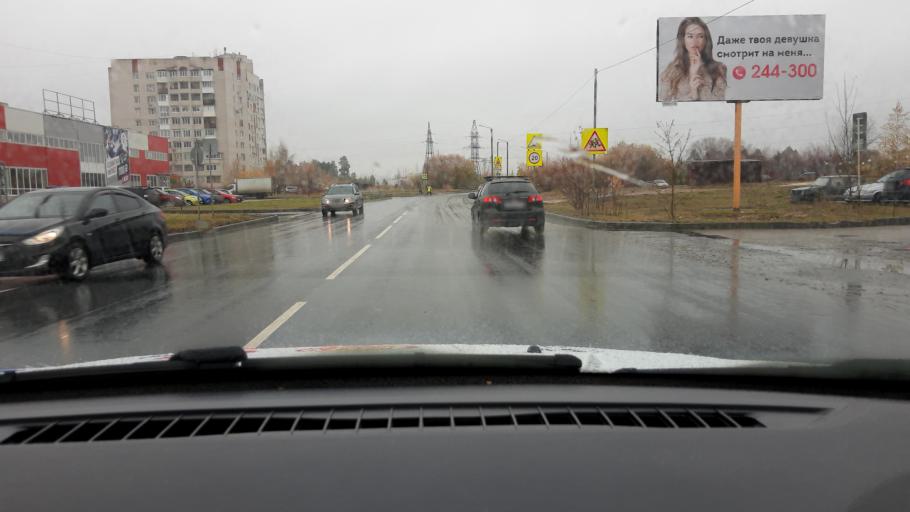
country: RU
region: Nizjnij Novgorod
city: Dzerzhinsk
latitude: 56.2337
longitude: 43.4089
